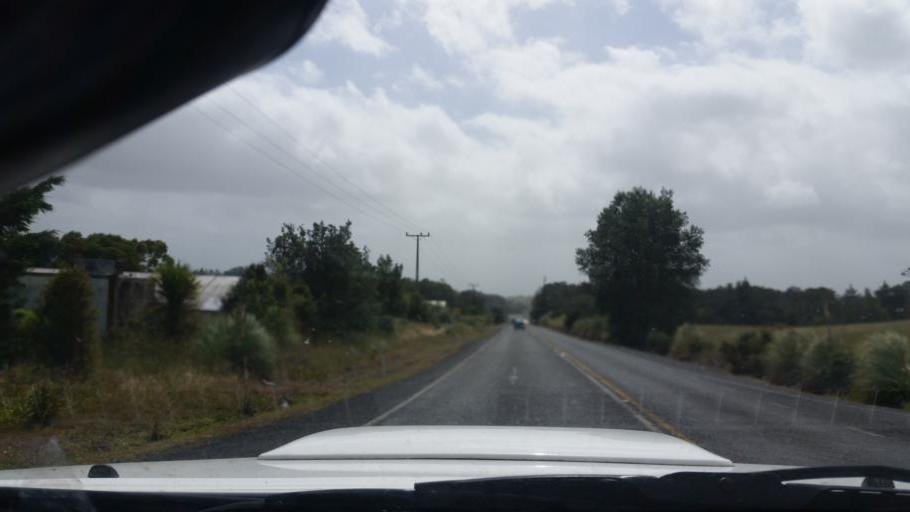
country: NZ
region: Northland
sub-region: Kaipara District
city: Dargaville
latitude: -36.1249
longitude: 174.1725
